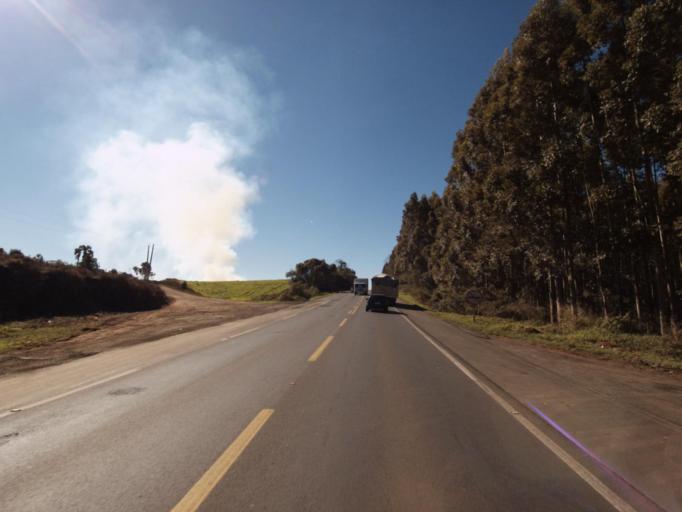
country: BR
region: Santa Catarina
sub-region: Xanxere
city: Xanxere
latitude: -26.9229
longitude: -52.4963
